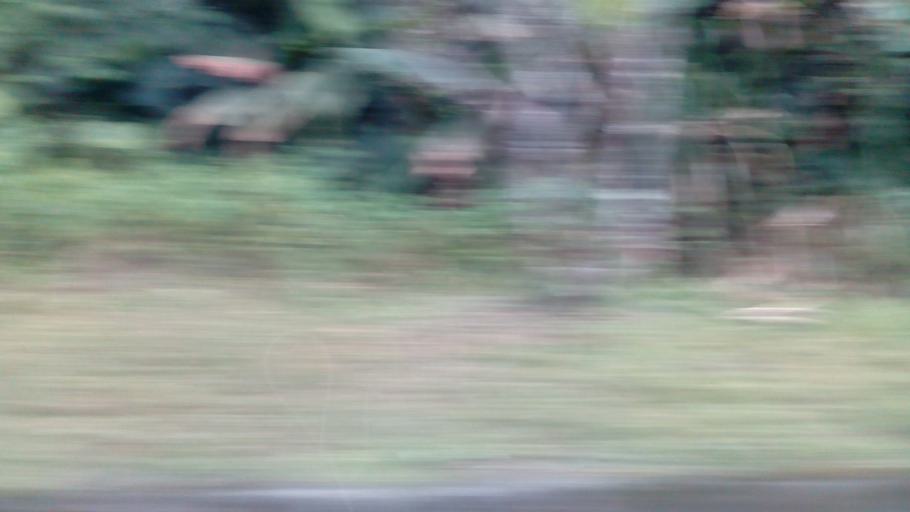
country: TW
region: Taiwan
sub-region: Yilan
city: Yilan
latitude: 24.5581
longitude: 121.4773
